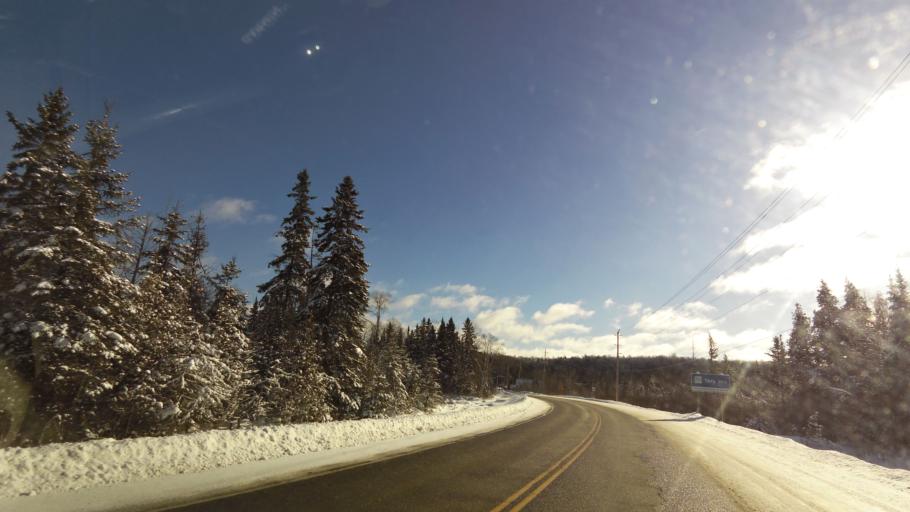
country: CA
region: Ontario
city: Bancroft
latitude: 44.9756
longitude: -78.2787
